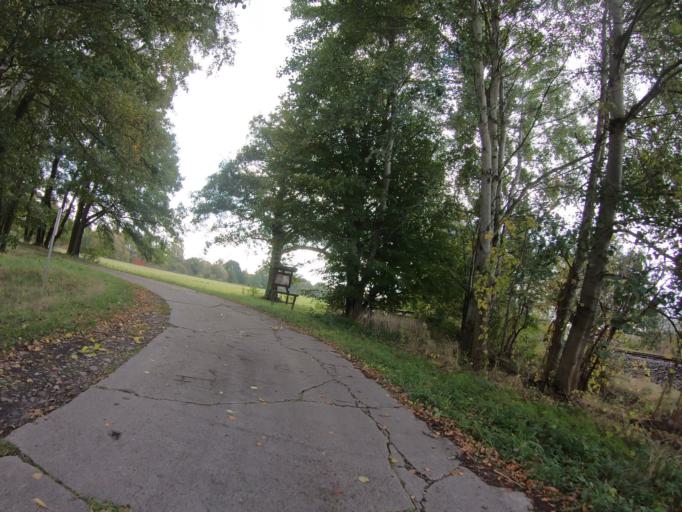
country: DE
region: Lower Saxony
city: Wahrenholz
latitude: 52.5788
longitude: 10.6106
